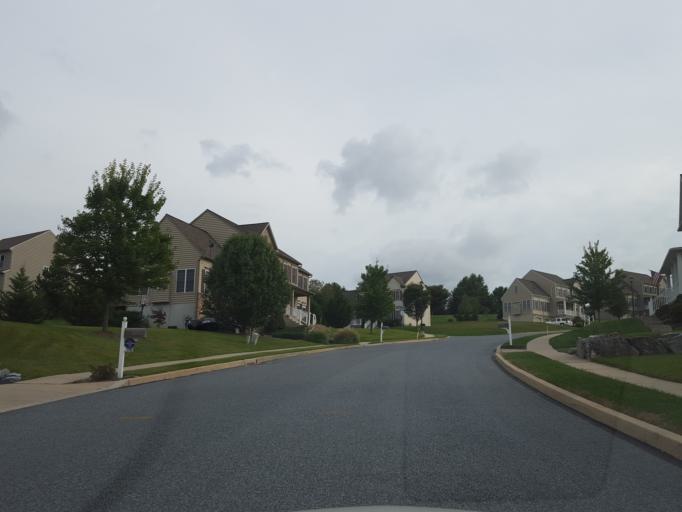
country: US
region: Pennsylvania
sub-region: York County
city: Yoe
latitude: 39.9343
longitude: -76.6504
